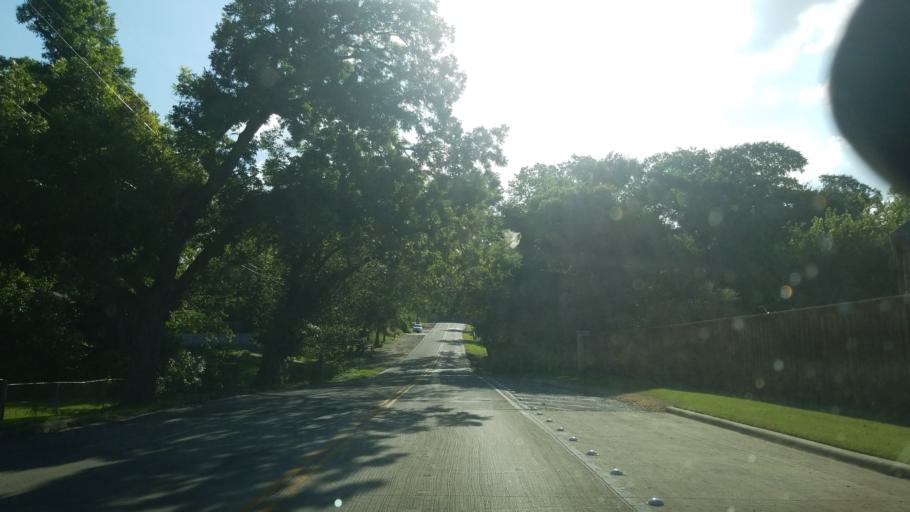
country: US
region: Texas
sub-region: Dallas County
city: Balch Springs
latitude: 32.7781
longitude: -96.7026
